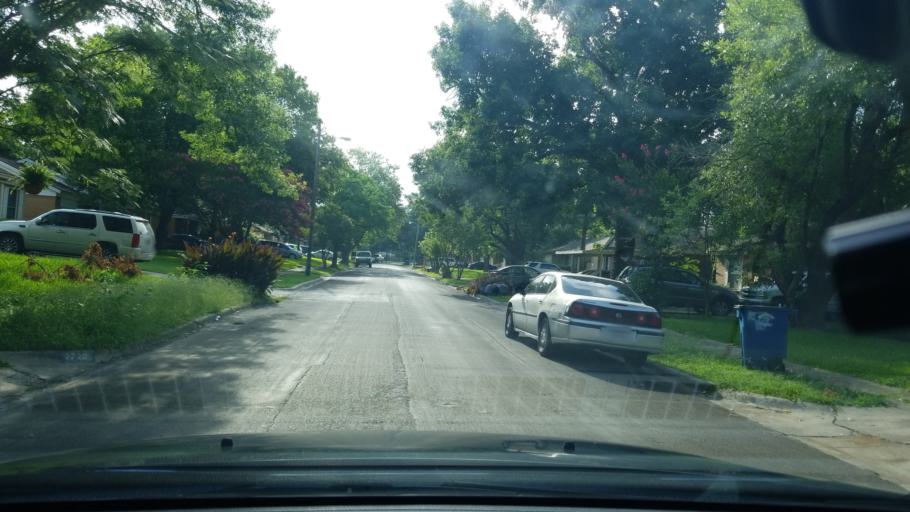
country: US
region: Texas
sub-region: Dallas County
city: Mesquite
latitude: 32.8233
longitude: -96.6671
